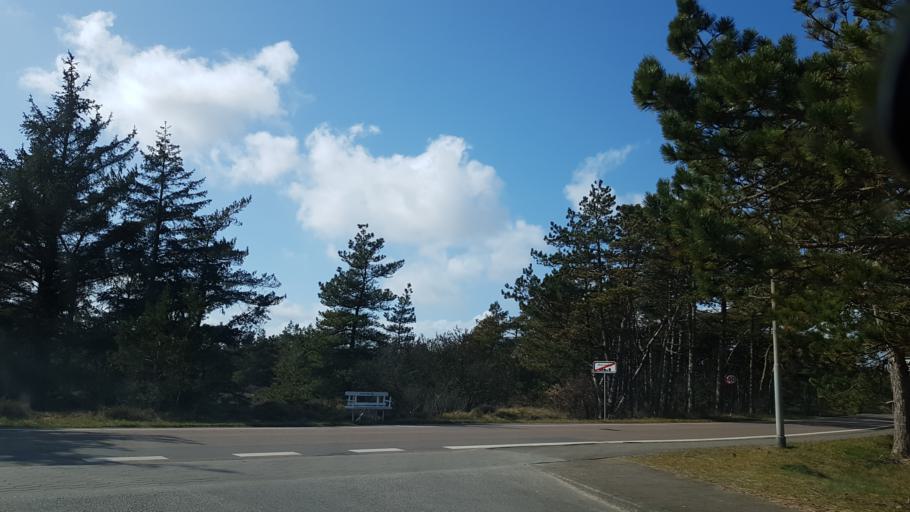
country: DE
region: Schleswig-Holstein
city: List
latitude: 55.0920
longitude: 8.5515
